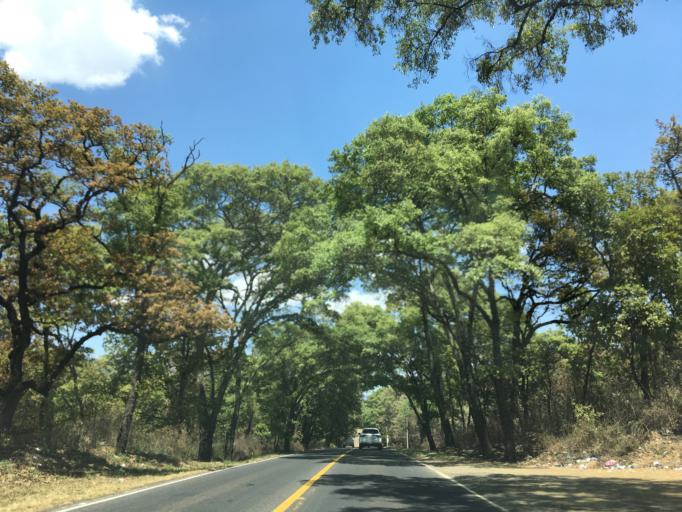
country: MX
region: Michoacan
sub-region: Chilchota
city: Tacuro (Santa Maria Tacuro)
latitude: 19.8099
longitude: -102.0272
